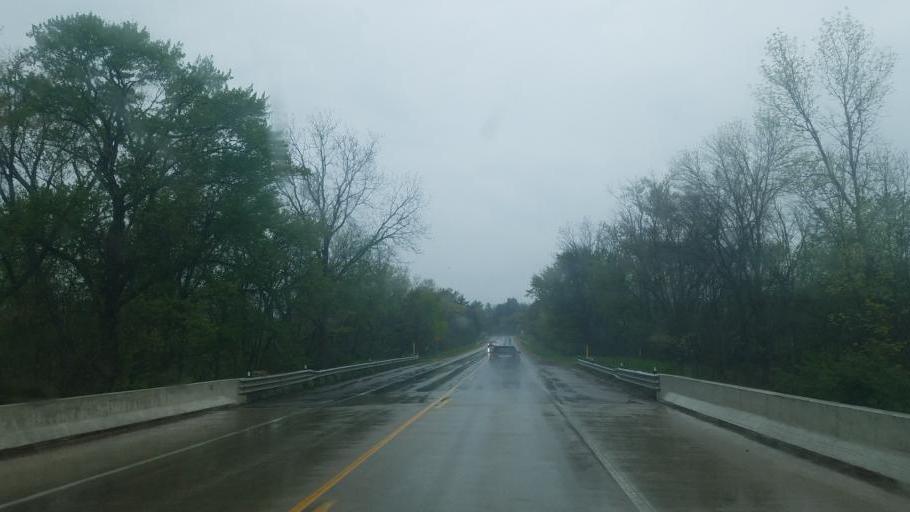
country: US
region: Wisconsin
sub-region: Sauk County
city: Reedsburg
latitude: 43.5785
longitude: -90.1135
